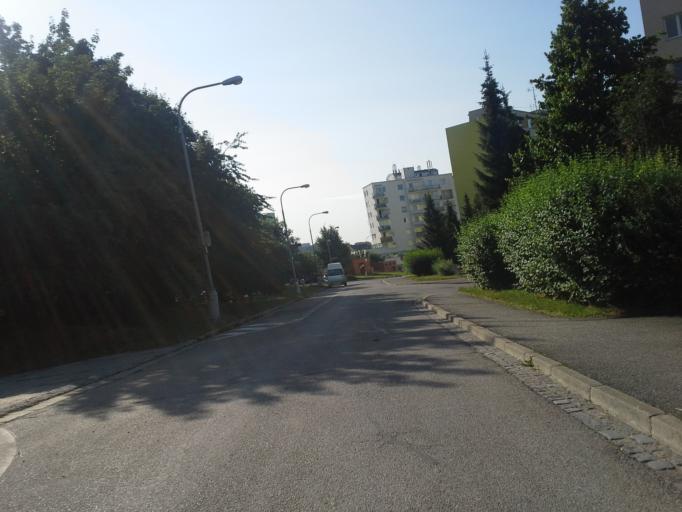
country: CZ
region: South Moravian
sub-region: Mesto Brno
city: Mokra Hora
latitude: 49.2397
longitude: 16.5819
